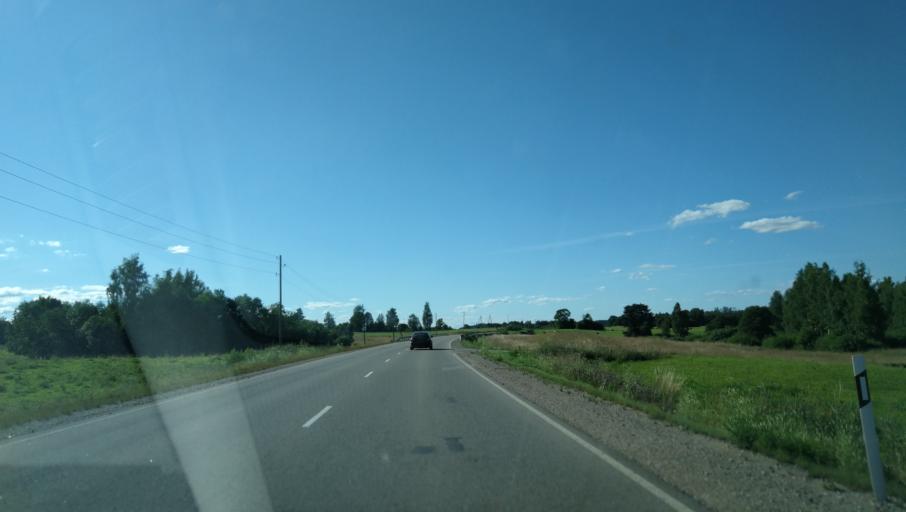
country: LV
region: Vecpiebalga
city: Vecpiebalga
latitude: 57.0819
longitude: 25.7493
